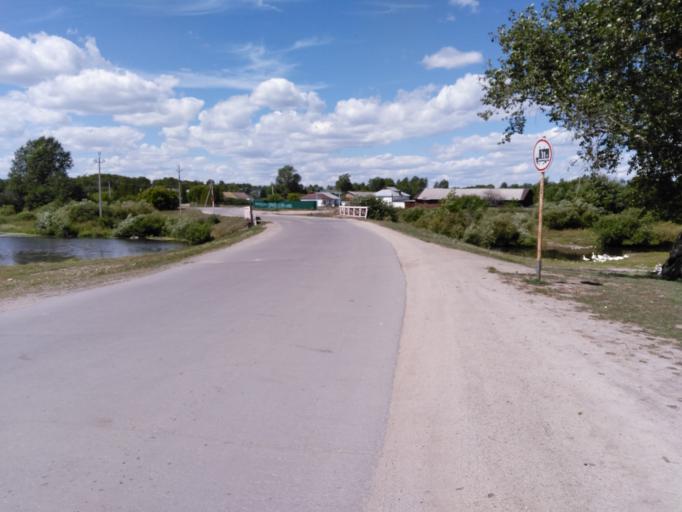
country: RU
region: Bashkortostan
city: Akhunovo
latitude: 54.2106
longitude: 59.6044
